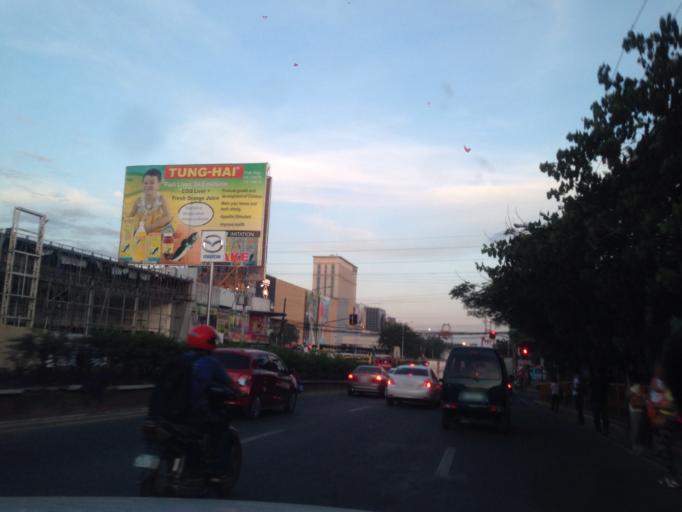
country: PH
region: Central Visayas
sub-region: Cebu City
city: Baugo
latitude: 10.3130
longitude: 123.9156
